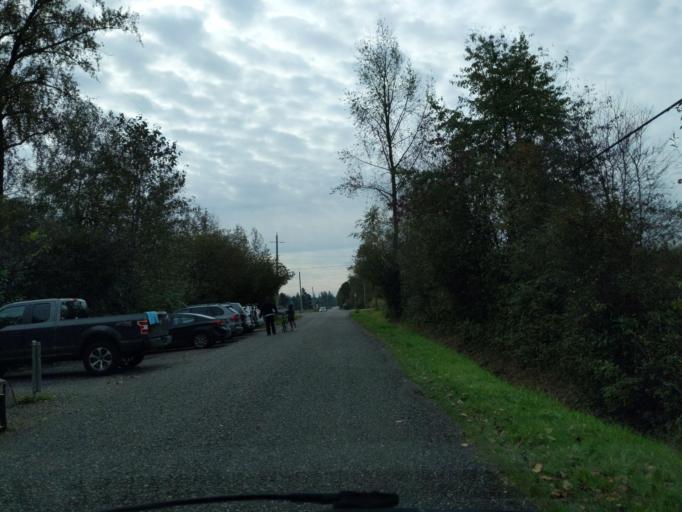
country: CA
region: British Columbia
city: Walnut Grove
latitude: 49.1983
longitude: -122.6444
